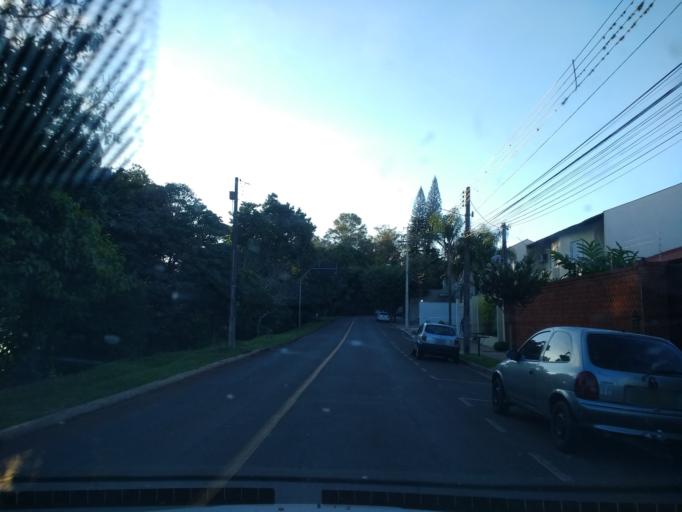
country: BR
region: Parana
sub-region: Londrina
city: Londrina
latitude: -23.3312
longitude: -51.1613
